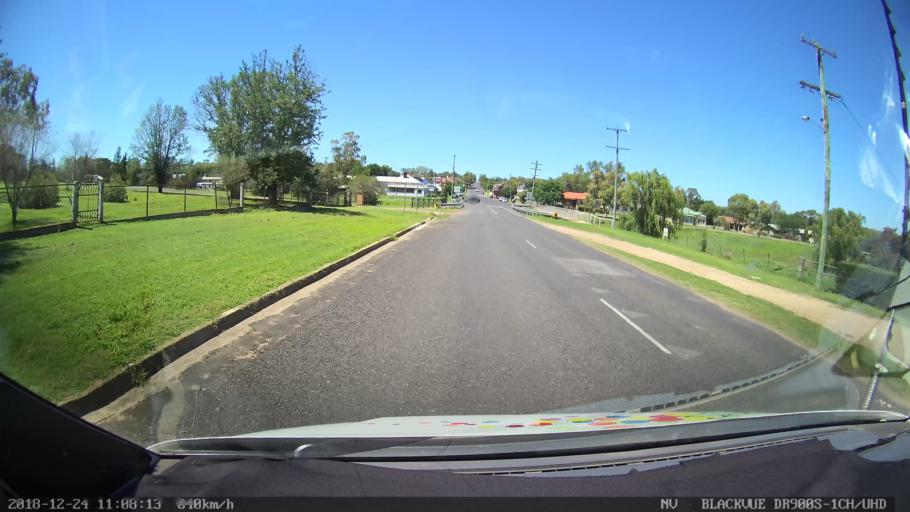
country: AU
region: New South Wales
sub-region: Upper Hunter Shire
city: Merriwa
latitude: -32.1363
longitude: 150.3564
